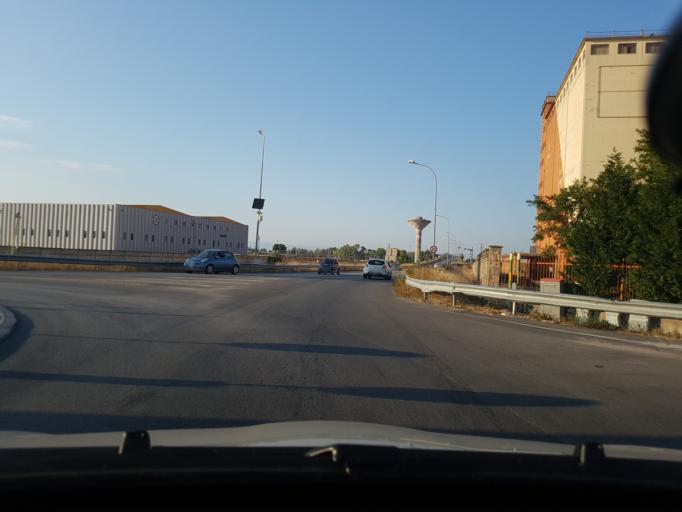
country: IT
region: Apulia
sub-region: Provincia di Foggia
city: Carapelle
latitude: 41.4023
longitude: 15.6501
